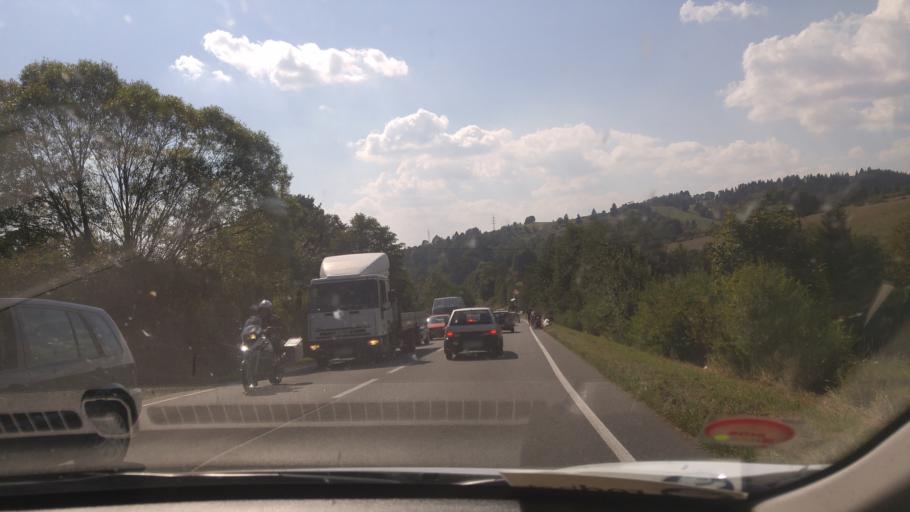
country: CZ
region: Olomoucky
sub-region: Okres Sumperk
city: Stare Mesto
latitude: 50.1574
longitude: 17.0145
